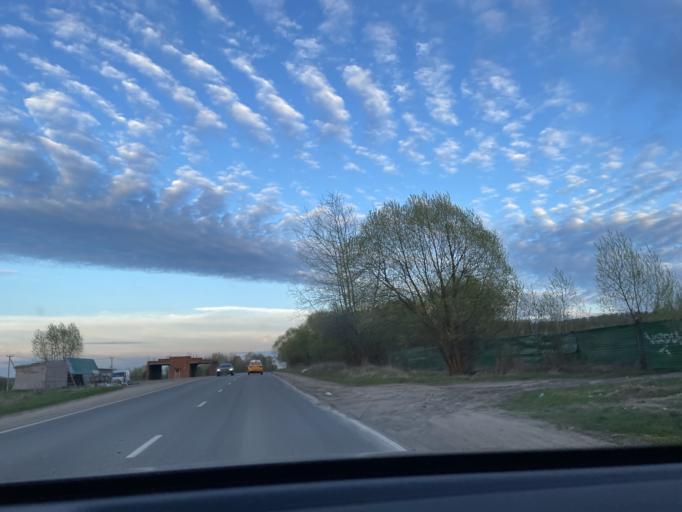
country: RU
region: Moskovskaya
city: Serpukhov
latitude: 54.8731
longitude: 37.4415
